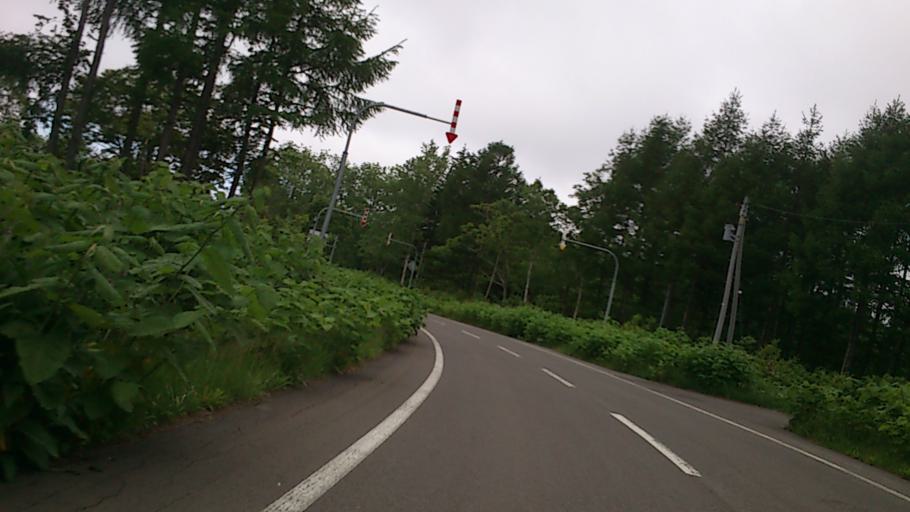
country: JP
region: Hokkaido
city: Niseko Town
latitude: 42.8533
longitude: 140.5715
